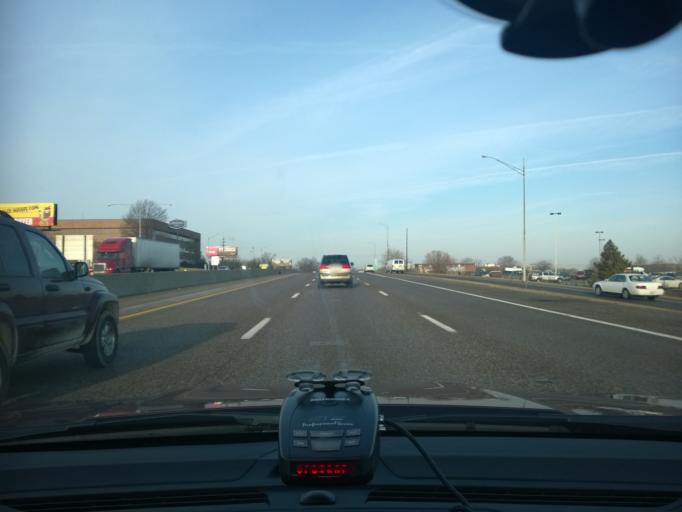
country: US
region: Missouri
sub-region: Saint Louis County
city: Saint Ann
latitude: 38.7399
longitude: -90.3696
